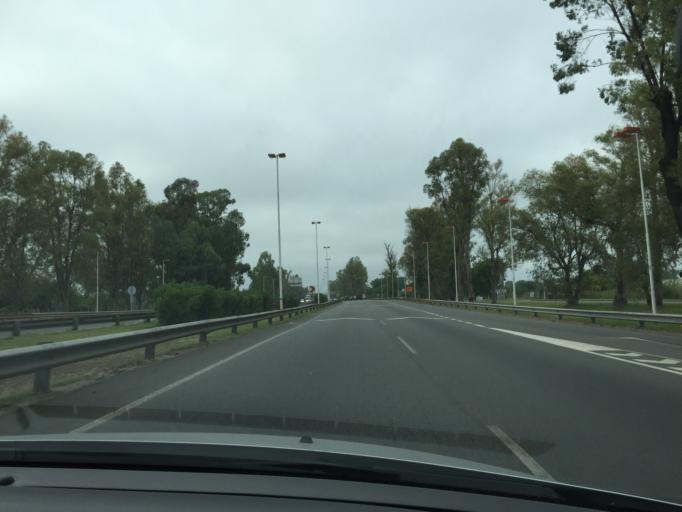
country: AR
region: Buenos Aires
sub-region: Partido de Ezeiza
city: Ezeiza
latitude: -34.8116
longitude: -58.5113
